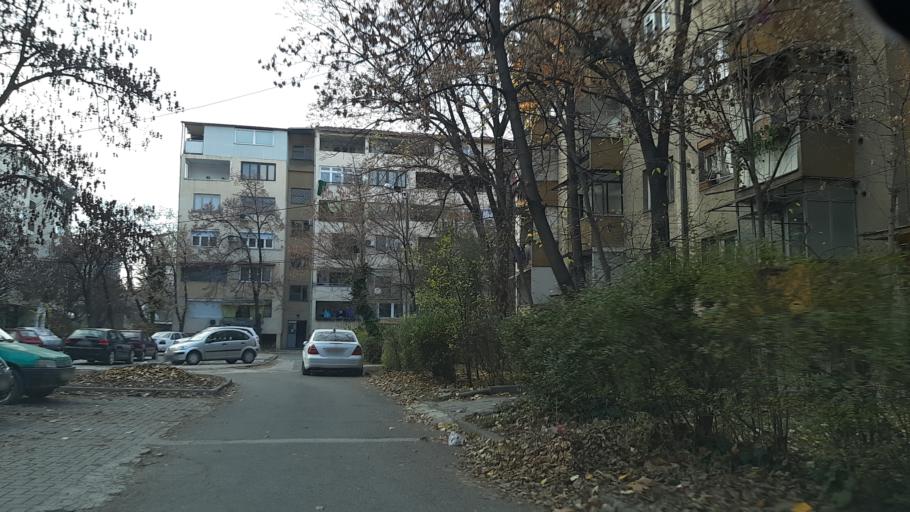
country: MK
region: Karpos
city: Skopje
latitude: 41.9793
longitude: 21.4467
